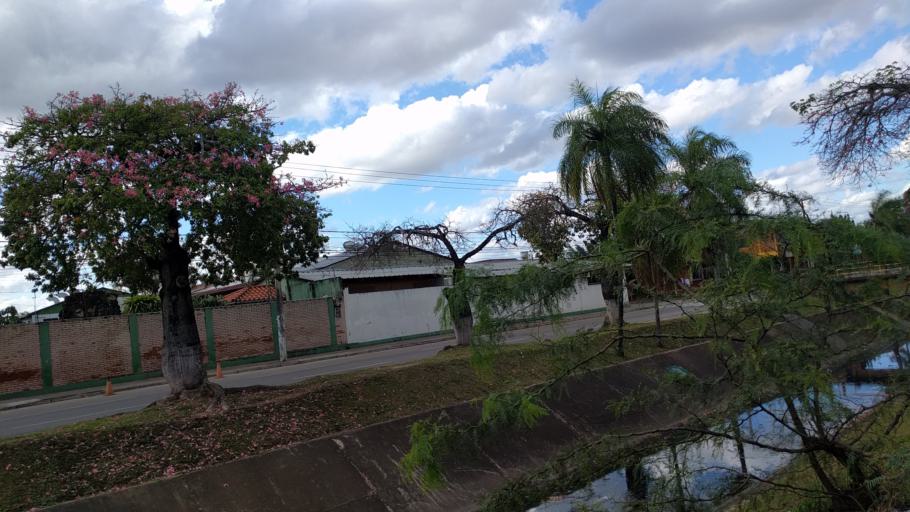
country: BO
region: Santa Cruz
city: Santa Cruz de la Sierra
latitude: -17.7780
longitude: -63.1627
